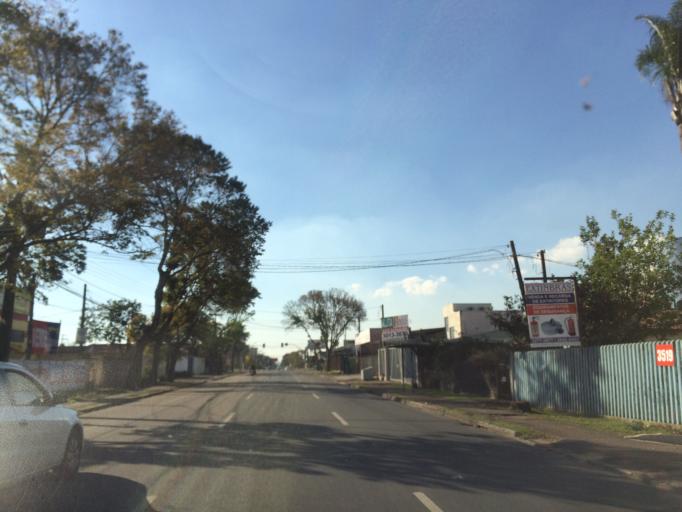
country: BR
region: Parana
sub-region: Sao Jose Dos Pinhais
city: Sao Jose dos Pinhais
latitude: -25.4966
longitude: -49.2386
